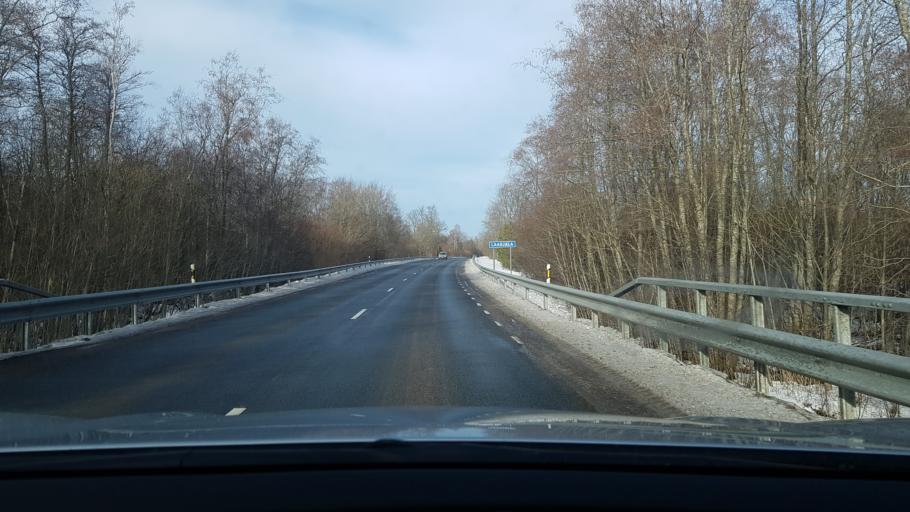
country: EE
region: Saare
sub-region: Kuressaare linn
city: Kuressaare
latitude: 58.3004
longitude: 22.5395
